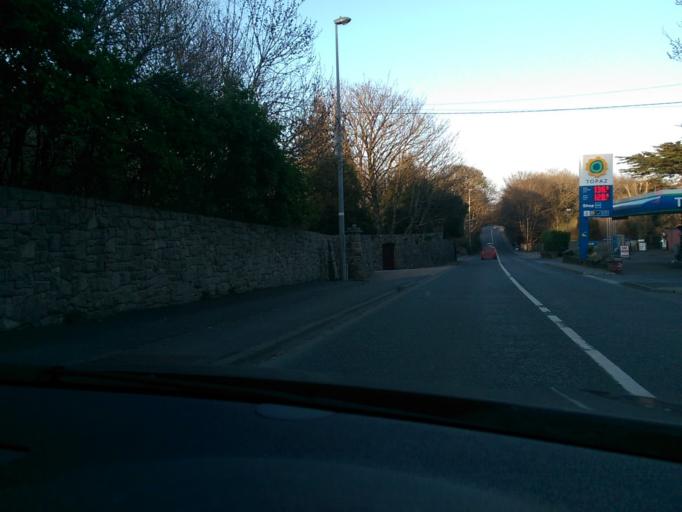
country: IE
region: Connaught
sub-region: County Galway
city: Bearna
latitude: 53.2590
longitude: -9.1304
